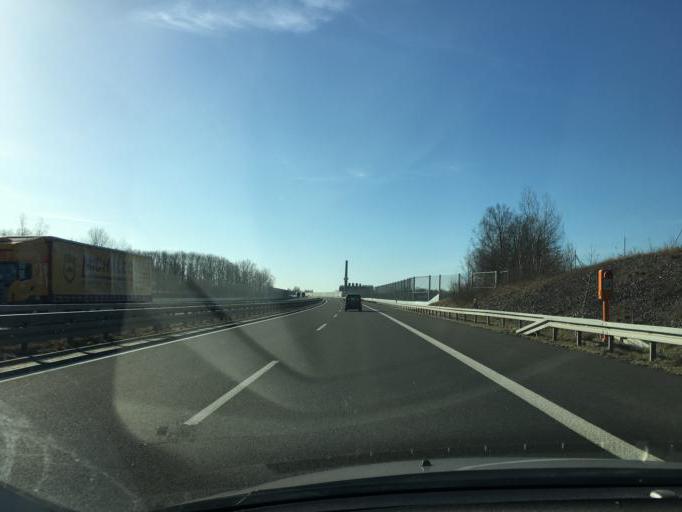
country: DE
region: Saxony
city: Borna
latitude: 51.1013
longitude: 12.5221
